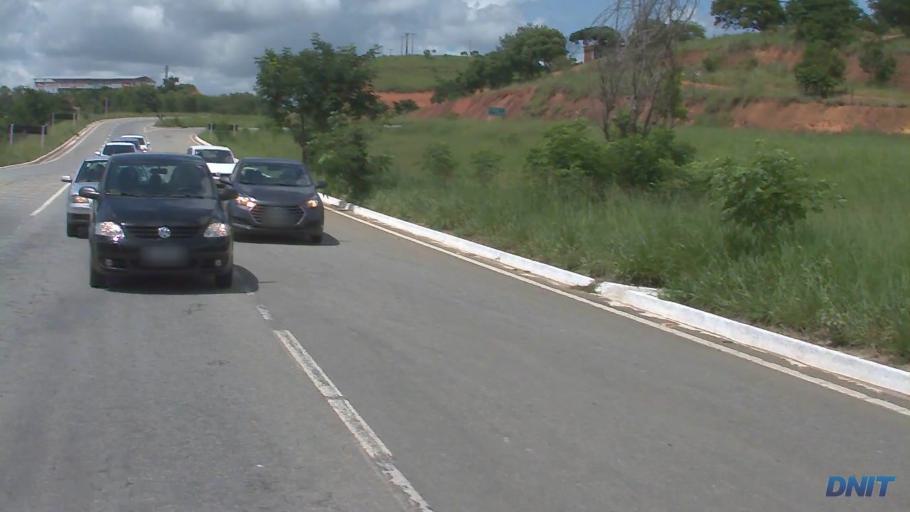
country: BR
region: Minas Gerais
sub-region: Governador Valadares
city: Governador Valadares
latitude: -18.9019
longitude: -42.0036
